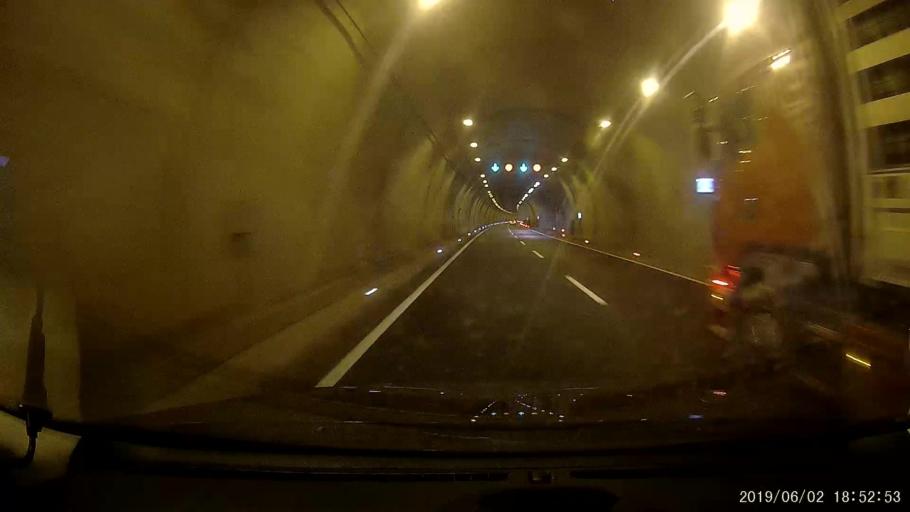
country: TR
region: Ordu
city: Ordu
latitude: 40.9856
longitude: 37.8218
